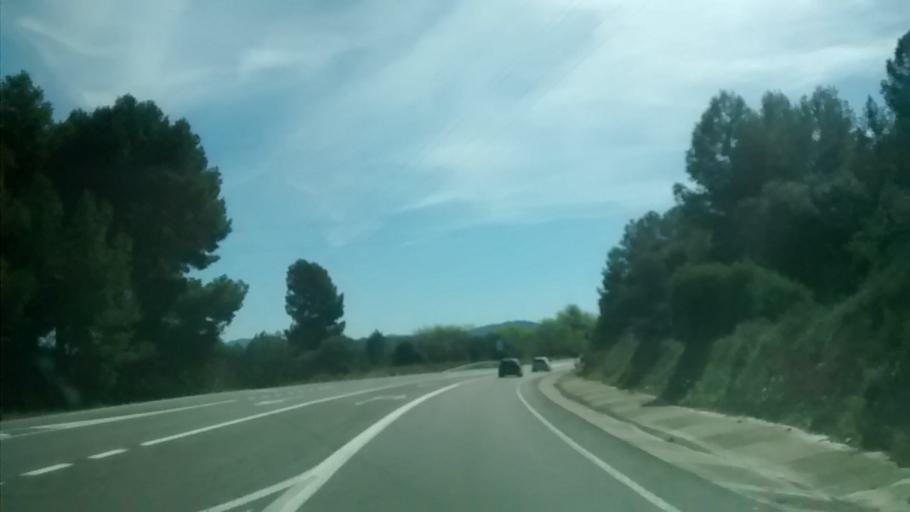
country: ES
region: Catalonia
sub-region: Provincia de Tarragona
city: Flix
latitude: 41.2229
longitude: 0.5454
